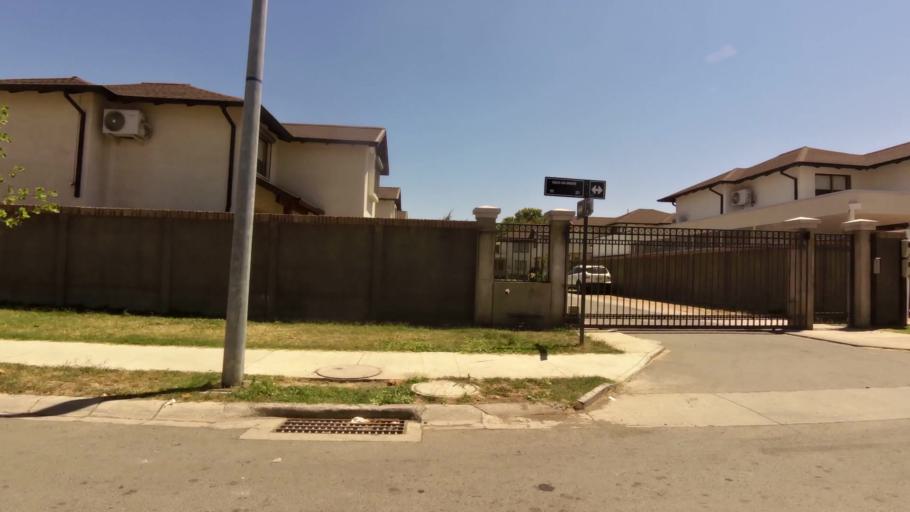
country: CL
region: Maule
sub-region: Provincia de Curico
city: Curico
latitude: -34.9855
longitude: -71.2123
